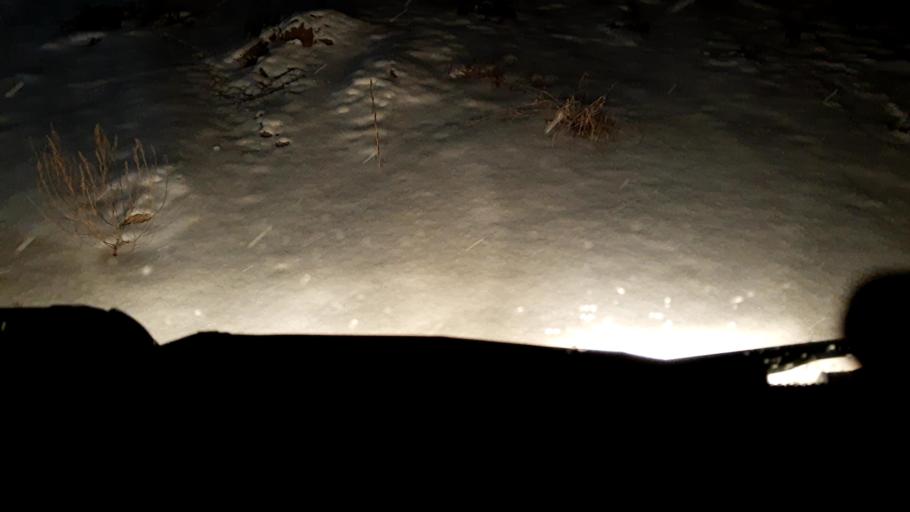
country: RU
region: Bashkortostan
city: Ufa
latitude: 54.7867
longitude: 56.0672
